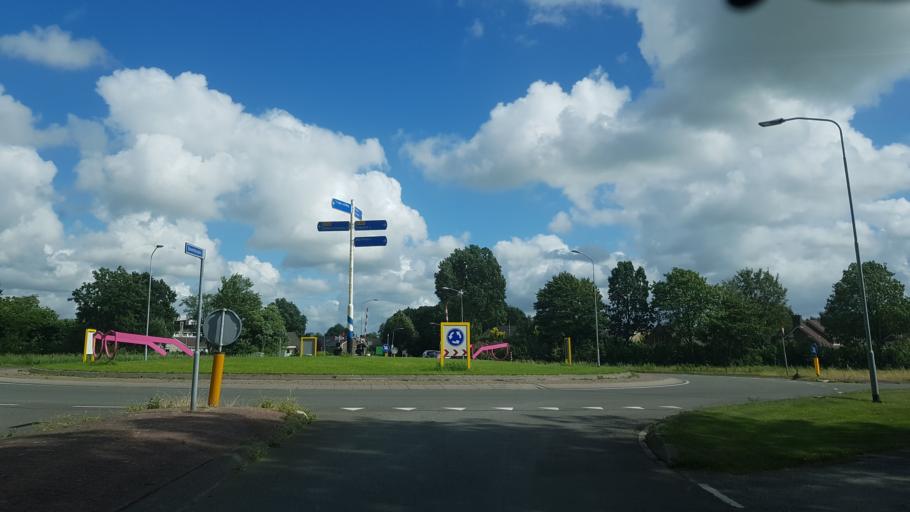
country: NL
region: Groningen
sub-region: Gemeente Bedum
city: Bedum
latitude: 53.4084
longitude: 6.6599
